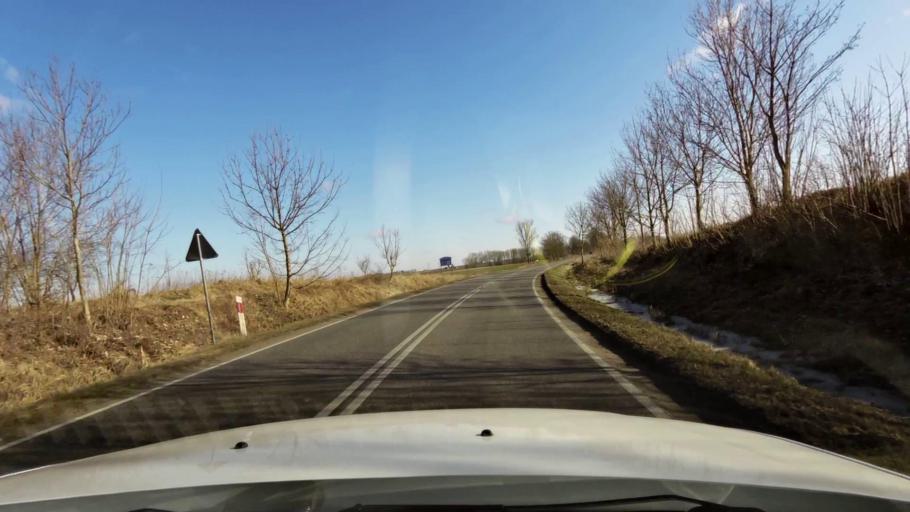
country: PL
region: West Pomeranian Voivodeship
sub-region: Powiat mysliborski
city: Barlinek
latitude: 52.9875
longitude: 15.1311
